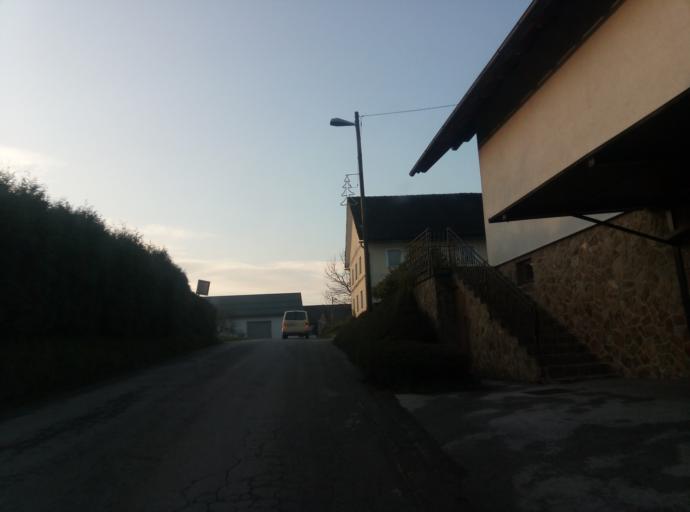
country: SI
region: Vodice
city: Vodice
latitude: 46.1763
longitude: 14.4846
